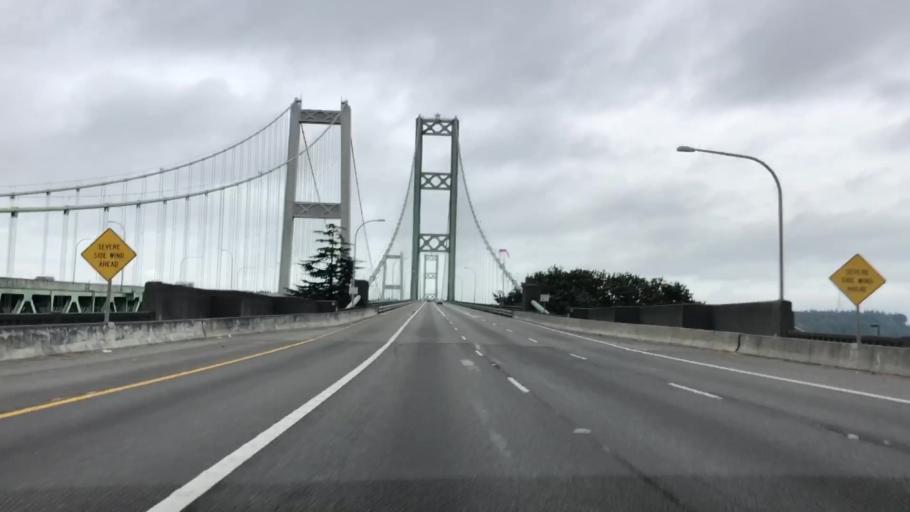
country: US
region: Washington
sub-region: Pierce County
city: University Place
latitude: 47.2626
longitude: -122.5432
